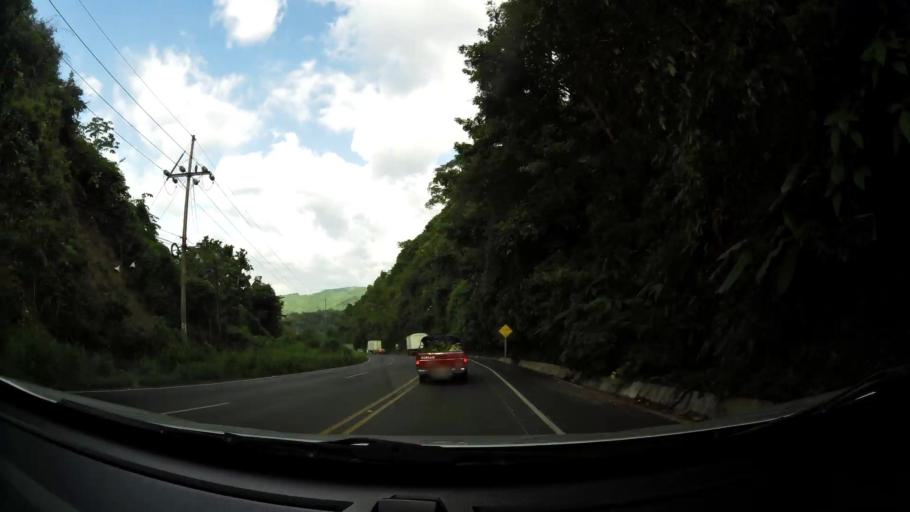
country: CR
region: Puntarenas
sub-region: Canton de Garabito
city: Jaco
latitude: 9.6998
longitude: -84.6393
